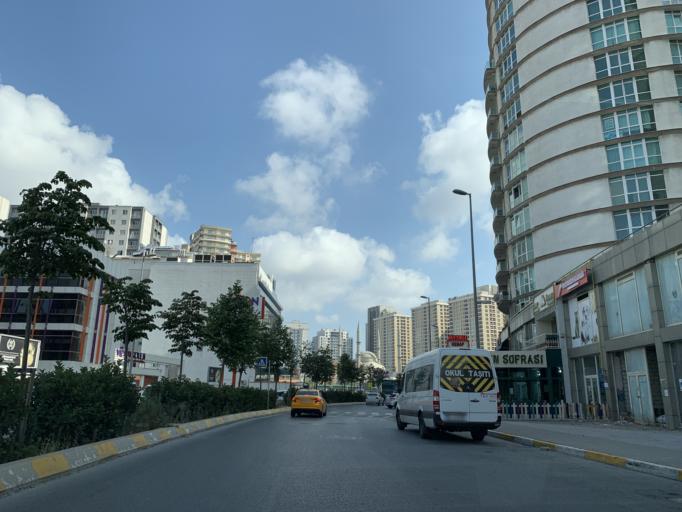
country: TR
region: Istanbul
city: Esenyurt
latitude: 41.0270
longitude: 28.6590
